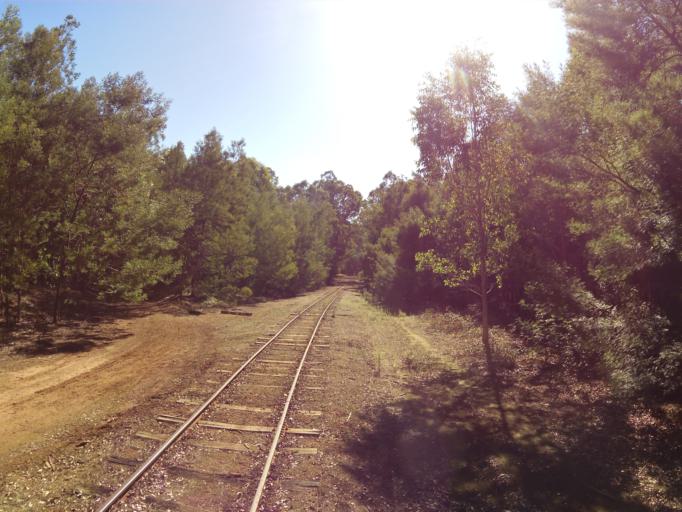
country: AU
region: Western Australia
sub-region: Waroona
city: Waroona
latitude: -32.7146
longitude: 116.0937
